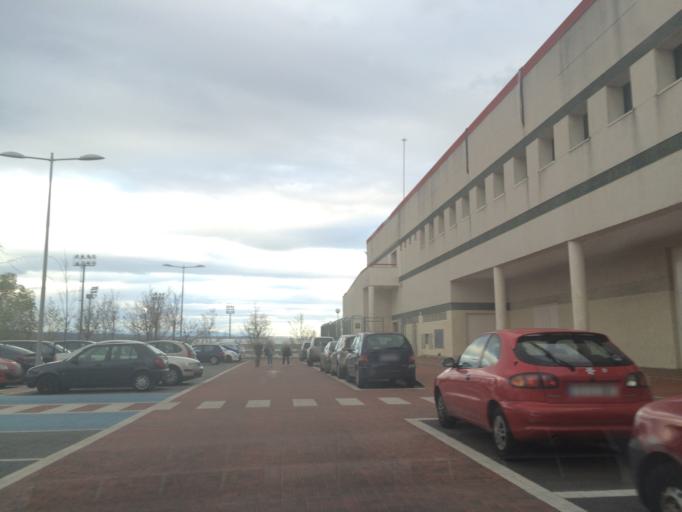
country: ES
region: Madrid
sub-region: Provincia de Madrid
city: Tres Cantos
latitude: 40.6056
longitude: -3.7061
